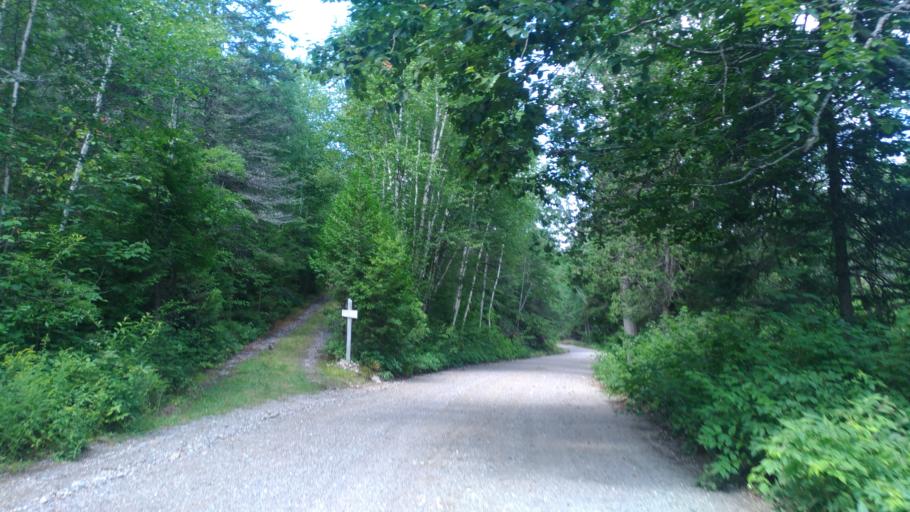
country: CA
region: Ontario
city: Rayside-Balfour
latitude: 46.5896
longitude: -81.5474
